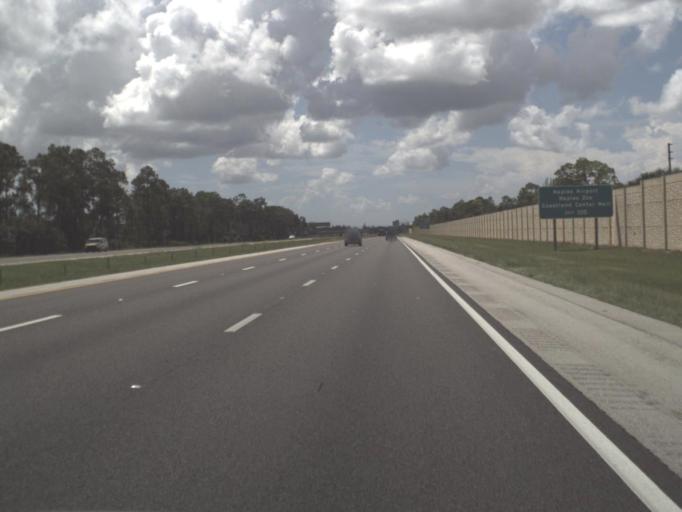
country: US
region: Florida
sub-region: Collier County
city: Golden Gate
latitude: 26.1925
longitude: -81.7360
